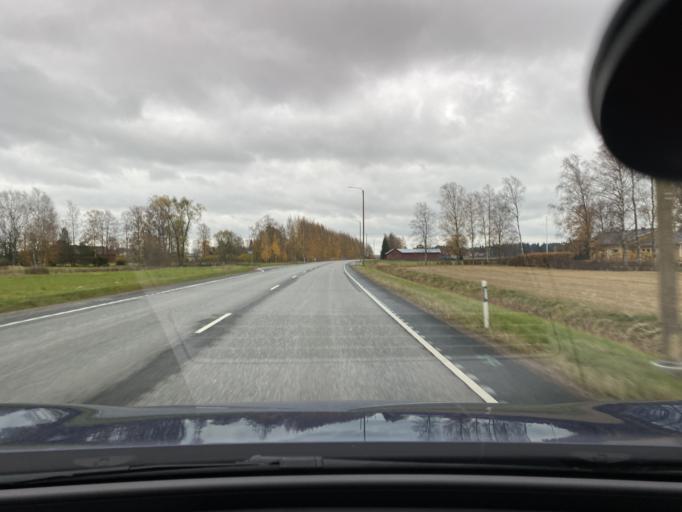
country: FI
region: Satakunta
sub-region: Rauma
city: Kiukainen
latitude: 61.1640
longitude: 22.0838
